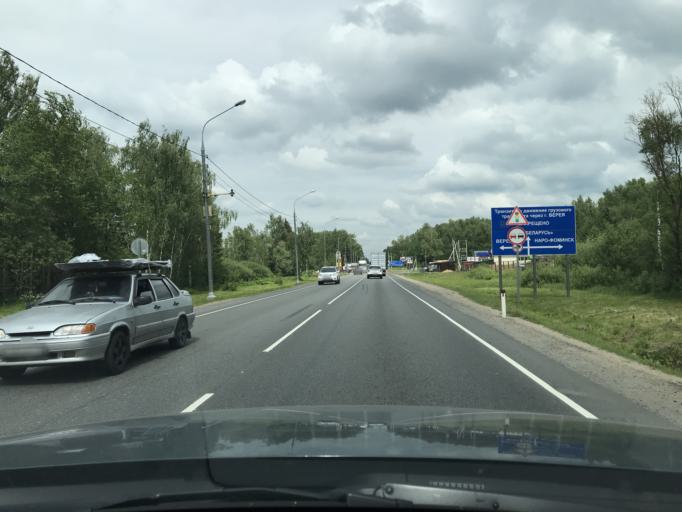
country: RU
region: Moskovskaya
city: Dorokhovo
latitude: 55.3824
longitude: 36.3998
